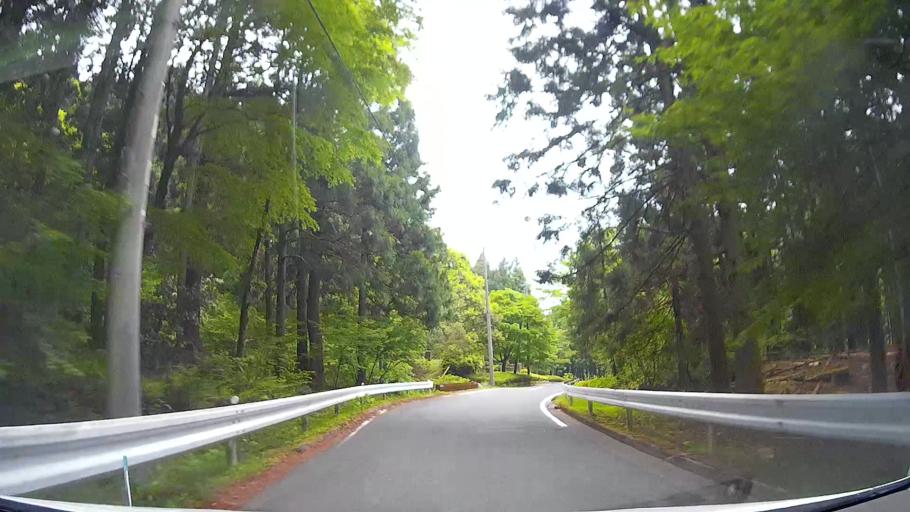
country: JP
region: Shizuoka
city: Ito
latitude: 34.9169
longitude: 139.0459
